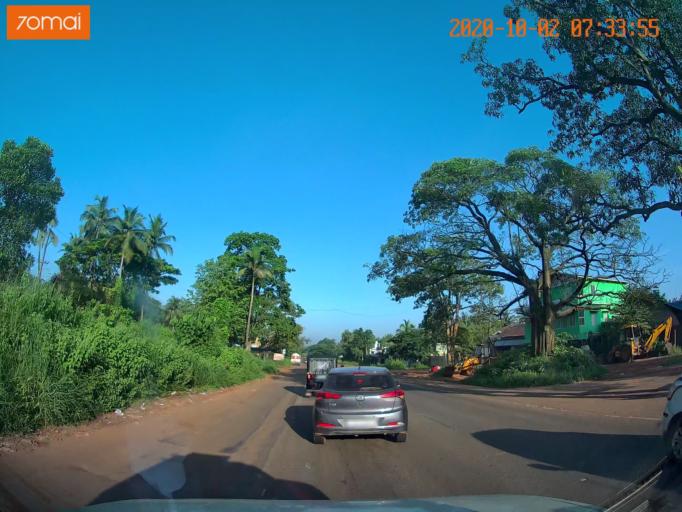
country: IN
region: Kerala
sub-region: Malappuram
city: Pariyapuram
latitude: 11.0615
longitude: 75.9345
